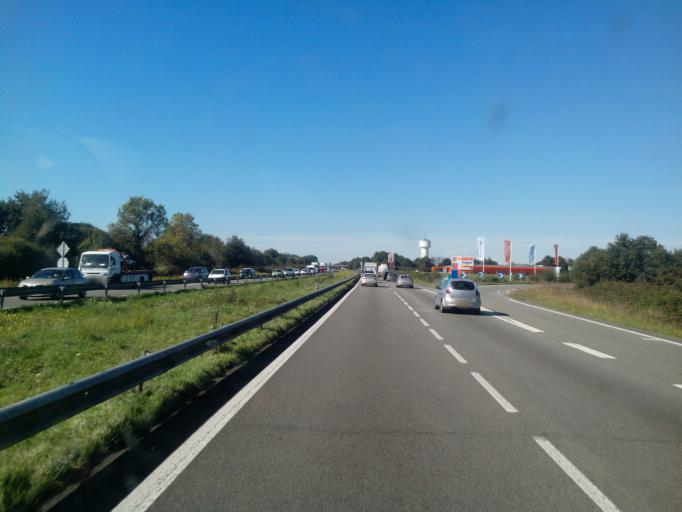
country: FR
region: Pays de la Loire
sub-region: Departement de la Loire-Atlantique
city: Sautron
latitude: 47.2743
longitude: -1.7191
